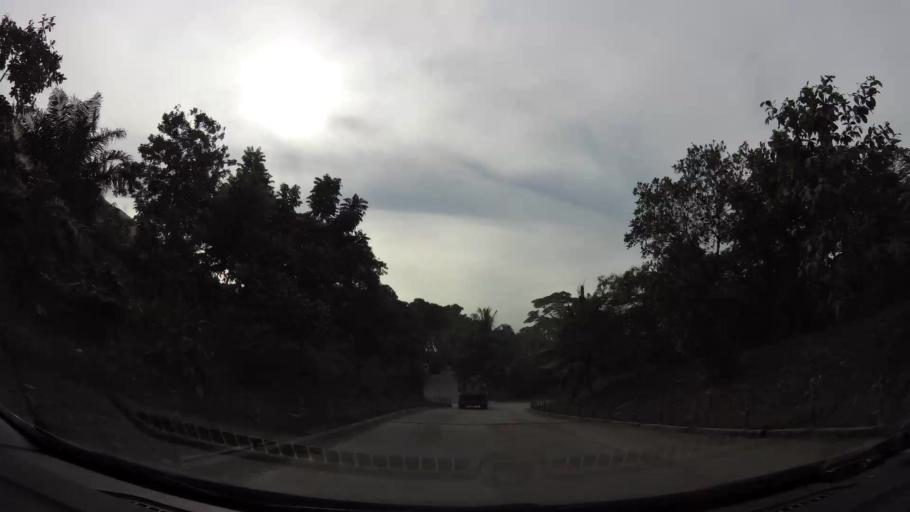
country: MY
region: Johor
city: Johor Bahru
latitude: 1.4380
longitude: 103.7071
